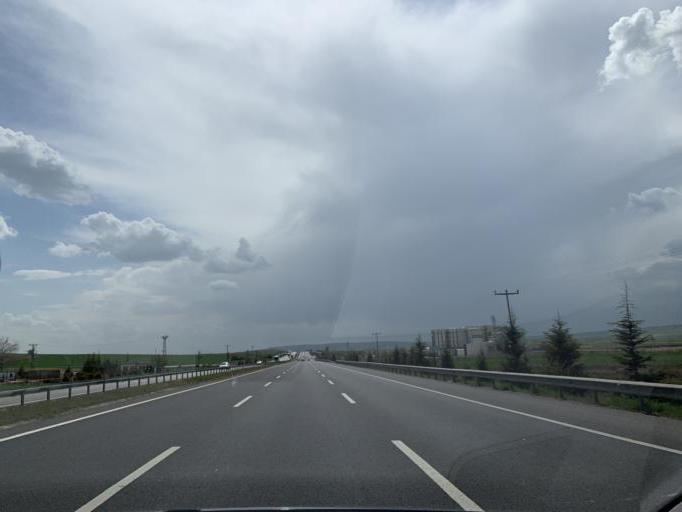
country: TR
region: Ankara
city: Temelli
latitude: 39.6873
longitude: 32.2490
